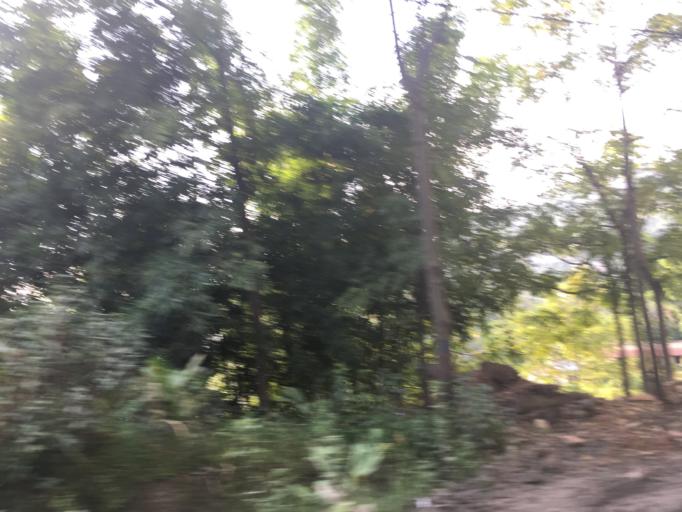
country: NP
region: Central Region
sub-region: Bagmati Zone
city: Bhaktapur
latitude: 27.6999
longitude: 85.4680
